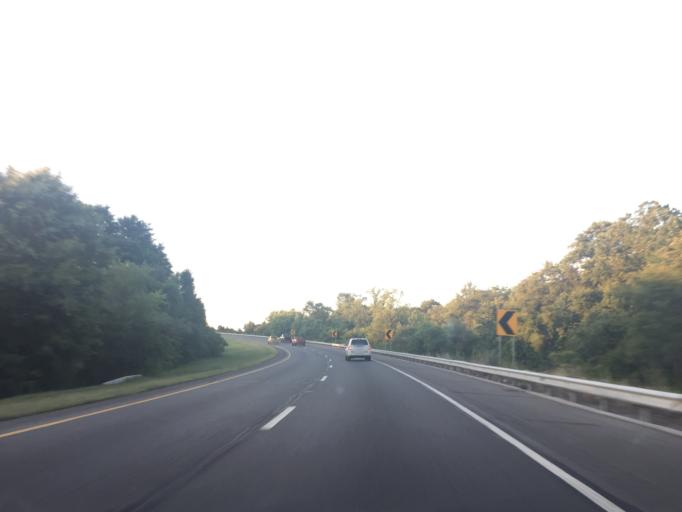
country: US
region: Delaware
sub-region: New Castle County
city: Bear
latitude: 39.6132
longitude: -75.6432
